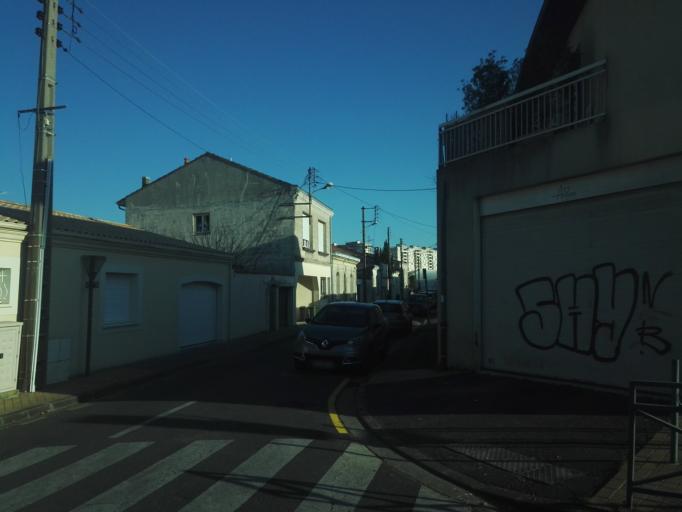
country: FR
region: Aquitaine
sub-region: Departement de la Gironde
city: Talence
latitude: 44.8142
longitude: -0.5813
